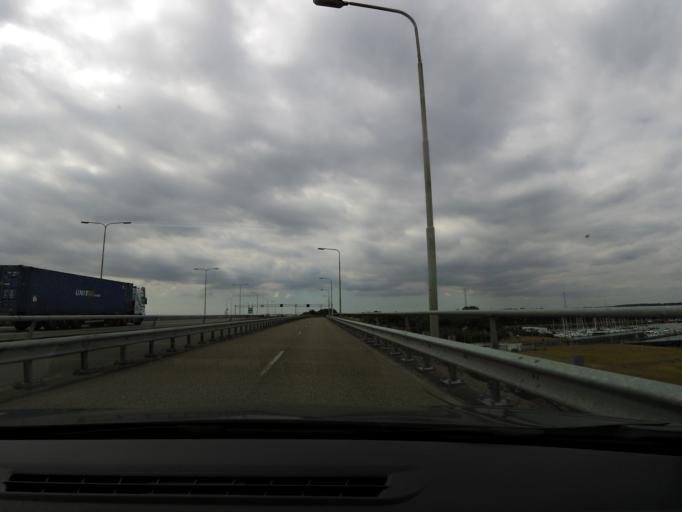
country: NL
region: North Brabant
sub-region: Gemeente Moerdijk
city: Willemstad
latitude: 51.6929
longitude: 4.4024
